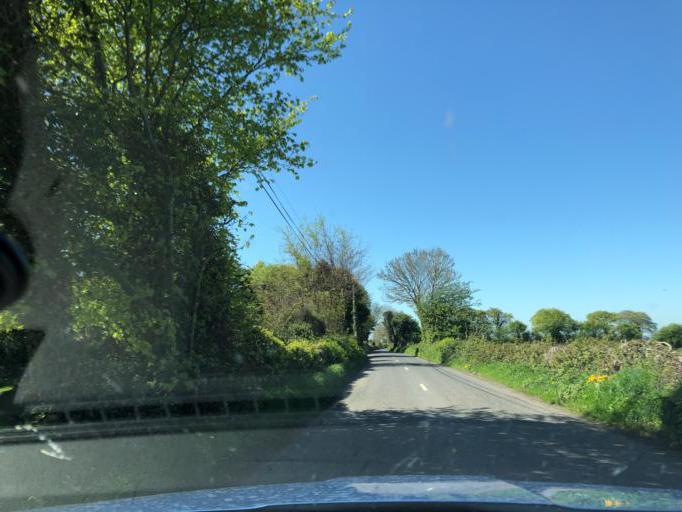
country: IE
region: Connaught
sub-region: County Galway
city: Portumna
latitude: 53.1738
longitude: -8.2069
